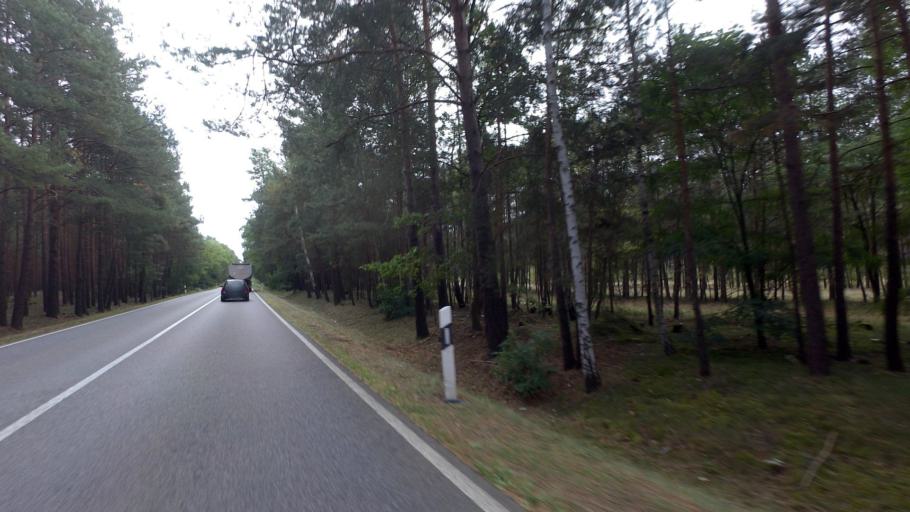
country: DE
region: Brandenburg
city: Kasel-Golzig
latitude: 51.9169
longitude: 13.6685
